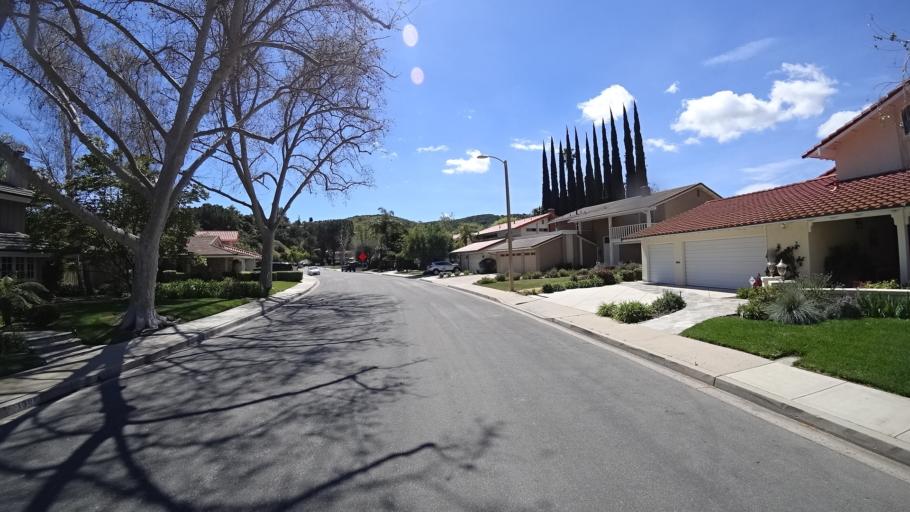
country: US
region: California
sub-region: Ventura County
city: Thousand Oaks
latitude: 34.1469
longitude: -118.8461
